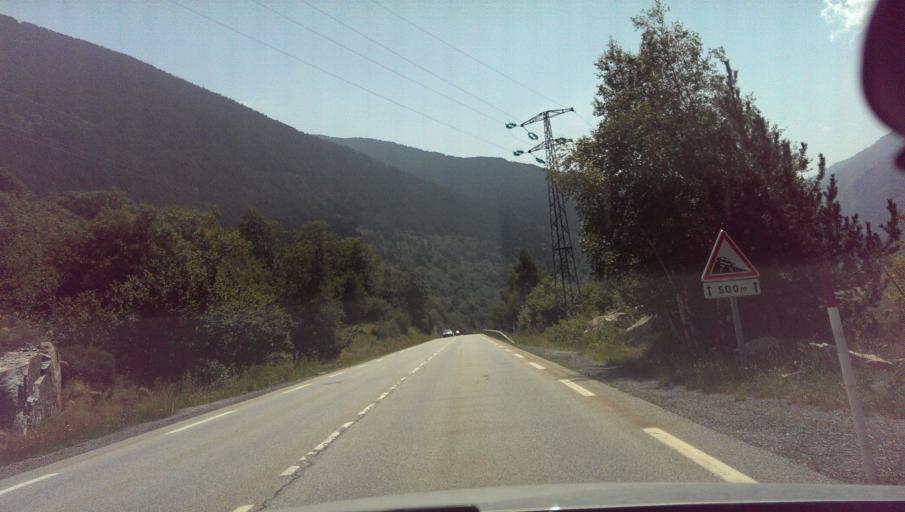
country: AD
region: Encamp
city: Pas de la Casa
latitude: 42.5306
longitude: 1.8223
